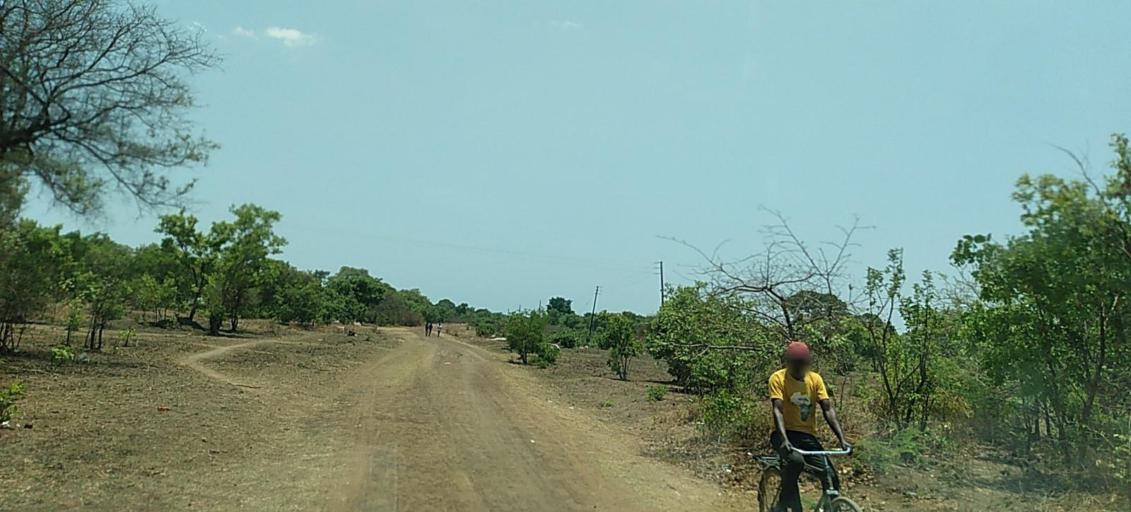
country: ZM
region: Copperbelt
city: Mpongwe
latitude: -13.8324
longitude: 27.8383
